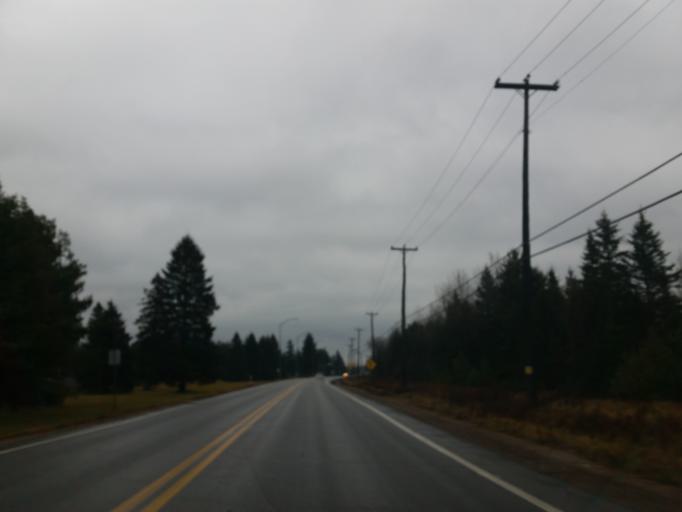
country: CA
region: Quebec
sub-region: Capitale-Nationale
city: Shannon
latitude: 46.8853
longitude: -71.4938
